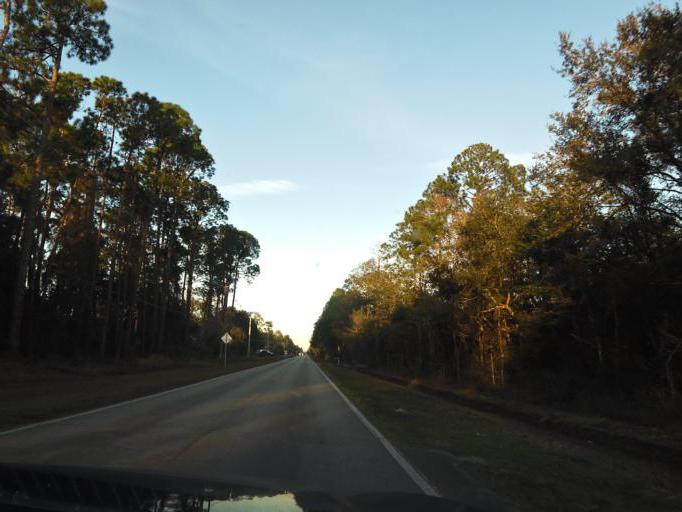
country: US
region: Florida
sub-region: Clay County
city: Green Cove Springs
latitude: 29.9386
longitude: -81.5652
